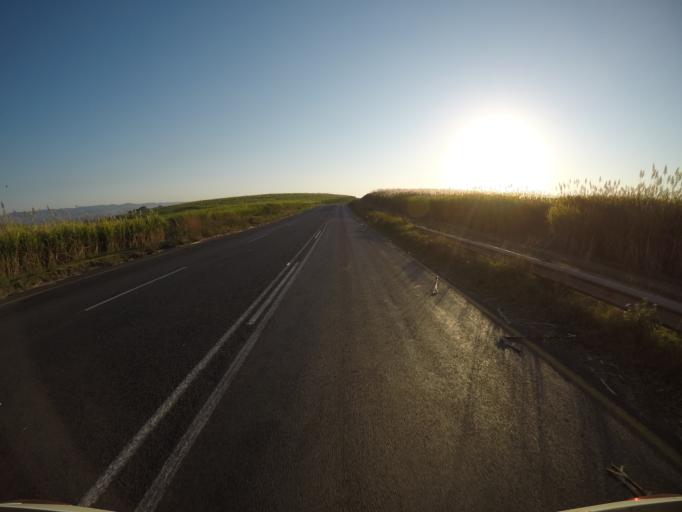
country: ZA
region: KwaZulu-Natal
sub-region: uThungulu District Municipality
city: eSikhawini
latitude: -28.9449
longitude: 31.7361
